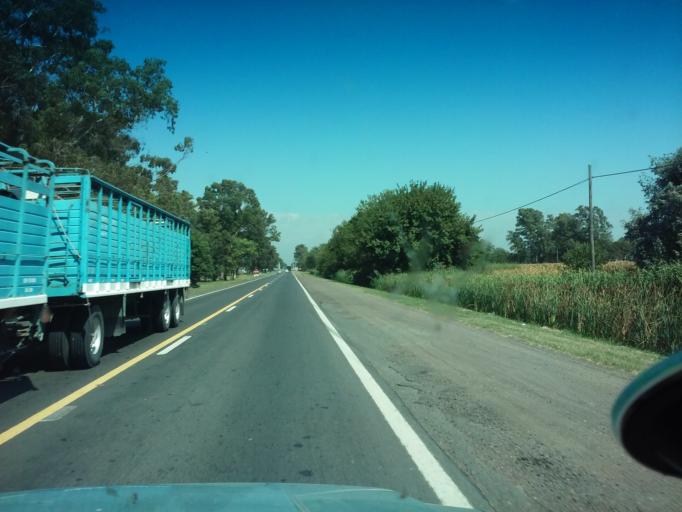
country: AR
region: Buenos Aires
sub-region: Partido de Nueve de Julio
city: Nueve de Julio
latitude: -35.4848
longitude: -60.8819
